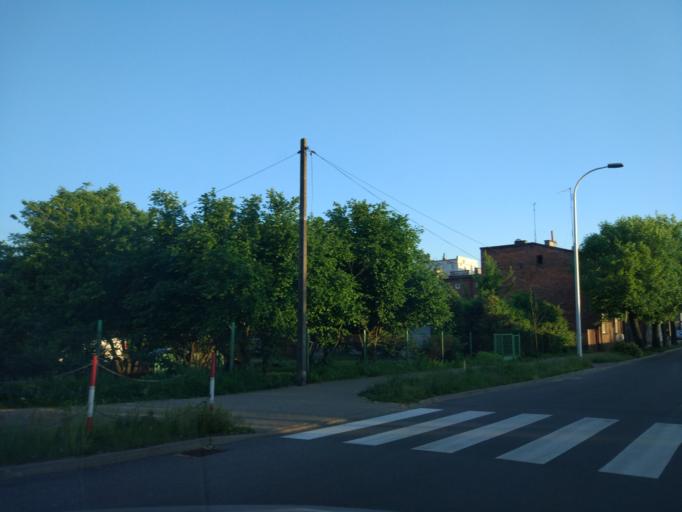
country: PL
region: Lodz Voivodeship
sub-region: Powiat kutnowski
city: Kutno
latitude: 52.2310
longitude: 19.3516
